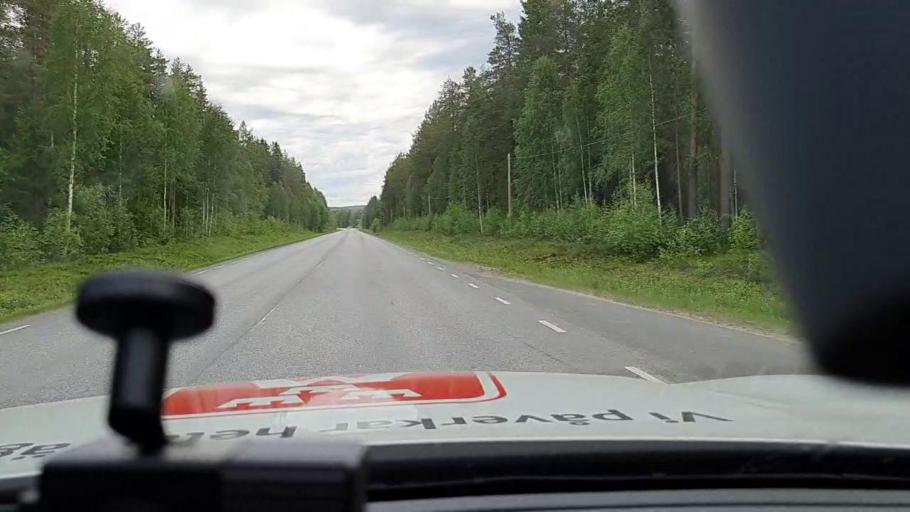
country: SE
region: Norrbotten
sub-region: Bodens Kommun
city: Boden
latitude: 65.8086
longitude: 21.6542
